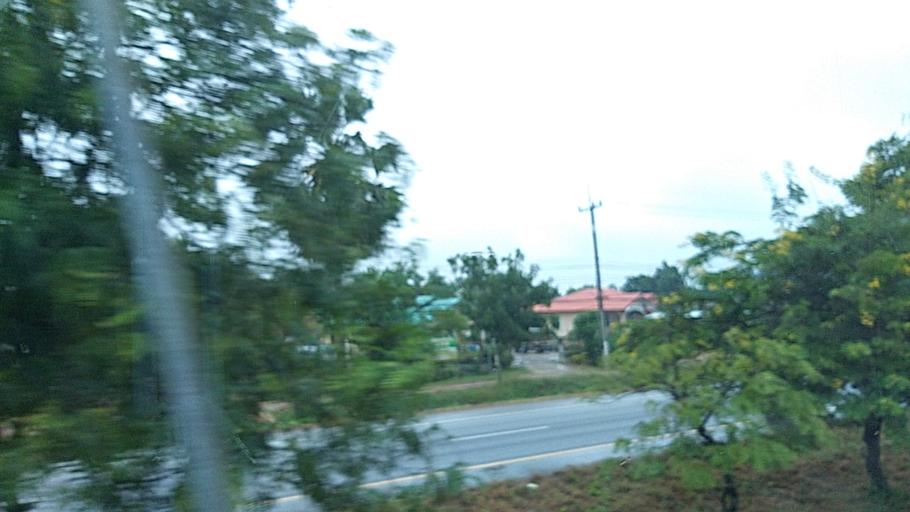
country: TH
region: Nakhon Ratchasima
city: Non Sung
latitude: 15.1543
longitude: 102.3280
